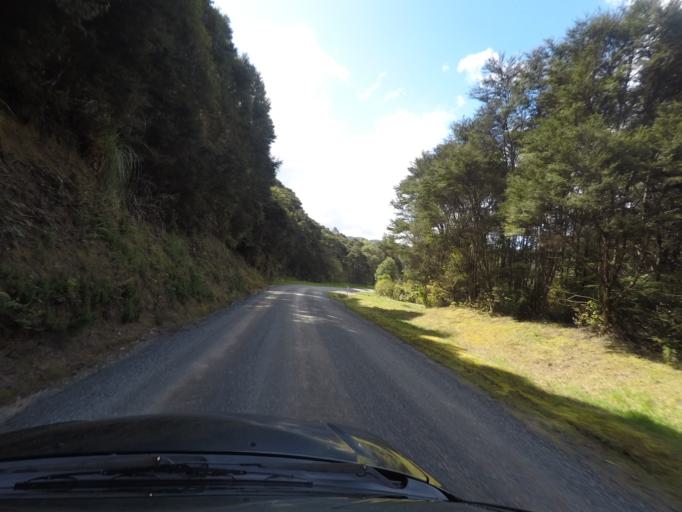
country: NZ
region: Auckland
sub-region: Auckland
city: Red Hill
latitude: -37.0947
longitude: 175.1515
